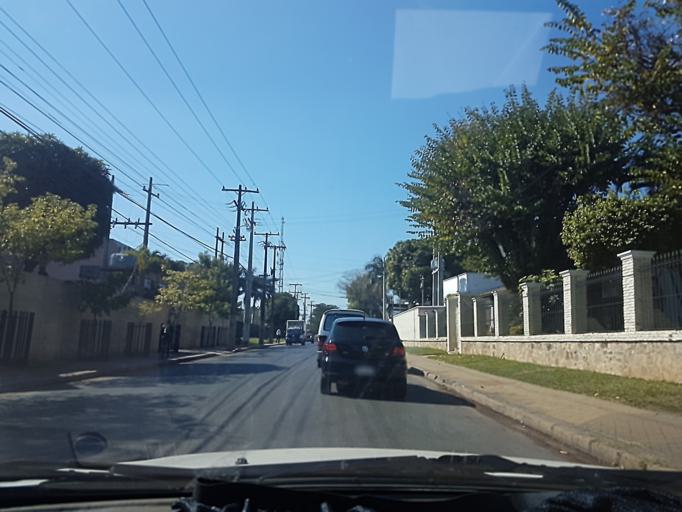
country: PY
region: Asuncion
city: Asuncion
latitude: -25.2580
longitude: -57.5698
